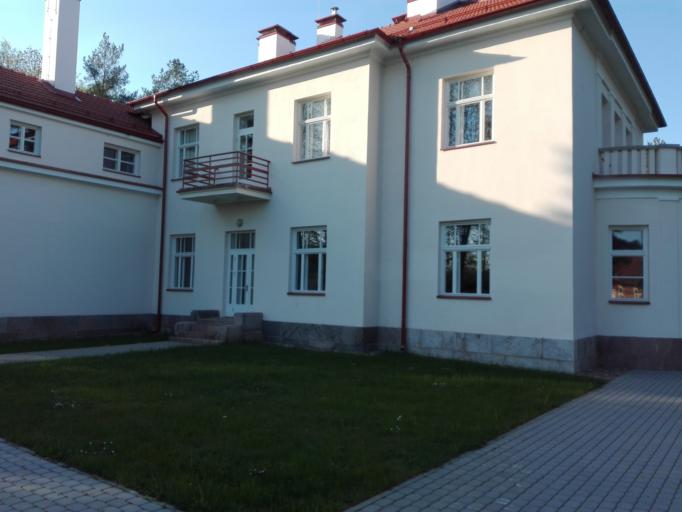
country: LT
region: Vilnius County
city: Ukmerge
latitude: 55.4250
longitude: 24.5638
